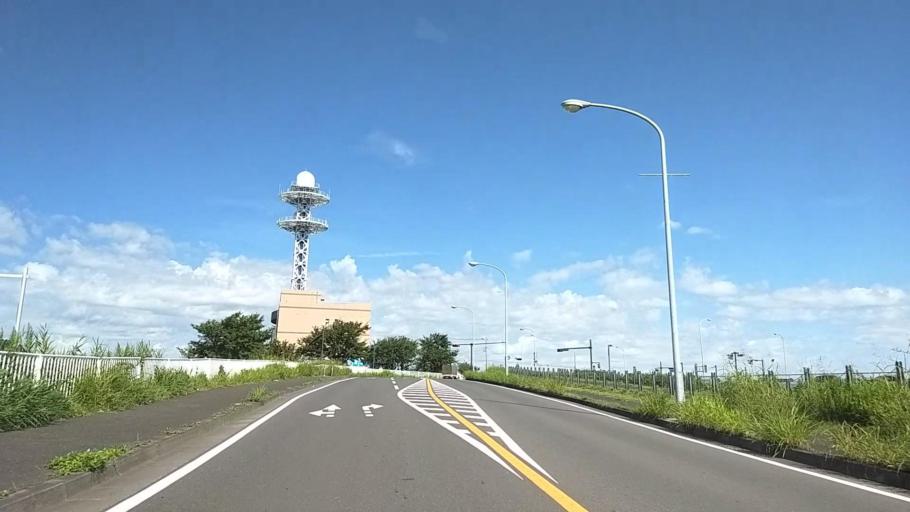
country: JP
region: Kanagawa
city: Yokohama
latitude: 35.5113
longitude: 139.6007
